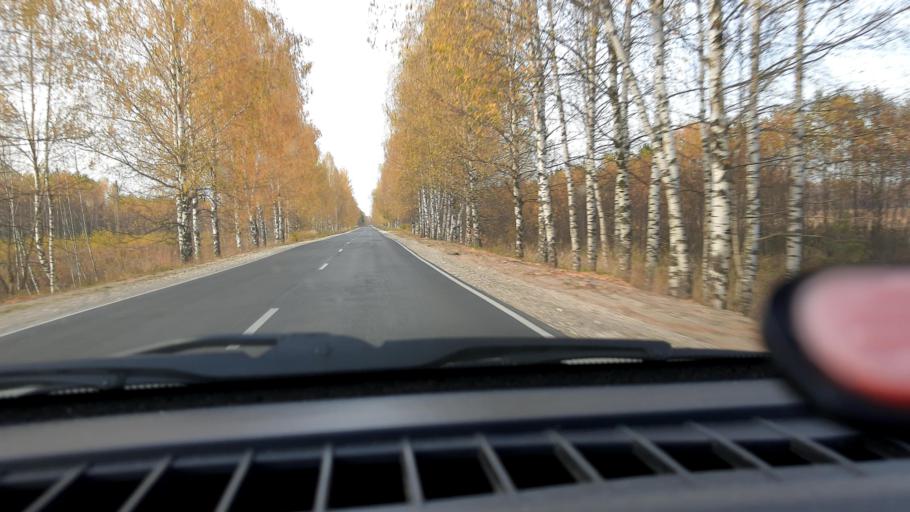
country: RU
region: Nizjnij Novgorod
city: Neklyudovo
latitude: 56.4916
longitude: 43.8599
